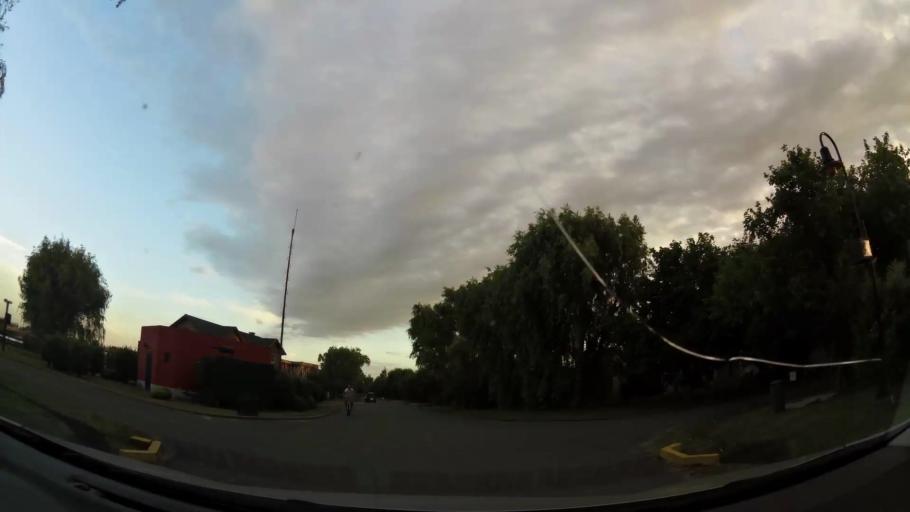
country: AR
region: Buenos Aires
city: Santa Catalina - Dique Lujan
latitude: -34.4410
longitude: -58.6557
